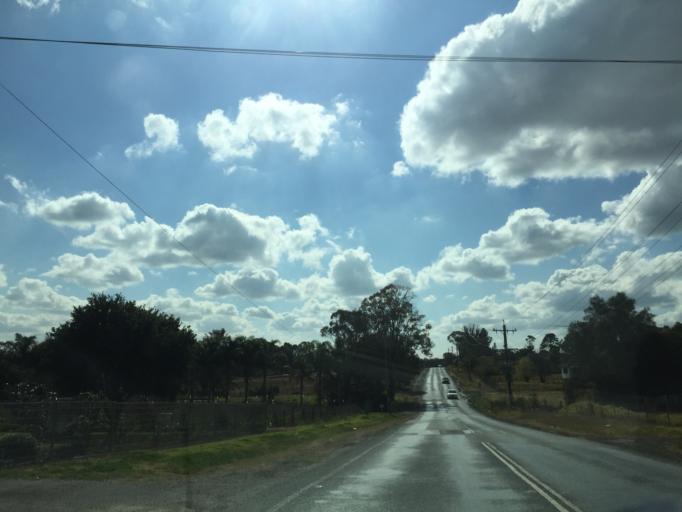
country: AU
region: New South Wales
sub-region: Blacktown
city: Rouse Hill
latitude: -33.7026
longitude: 150.8944
